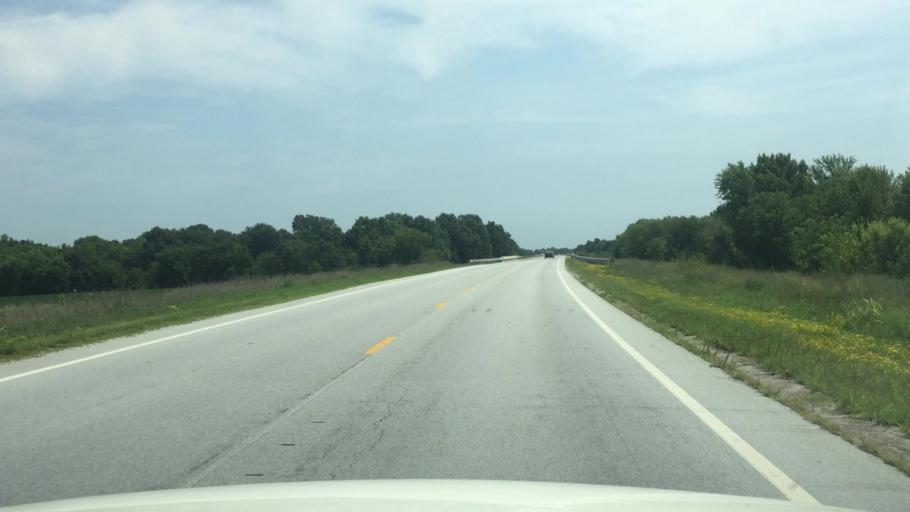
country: US
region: Kansas
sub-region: Labette County
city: Oswego
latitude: 37.1802
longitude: -94.9788
